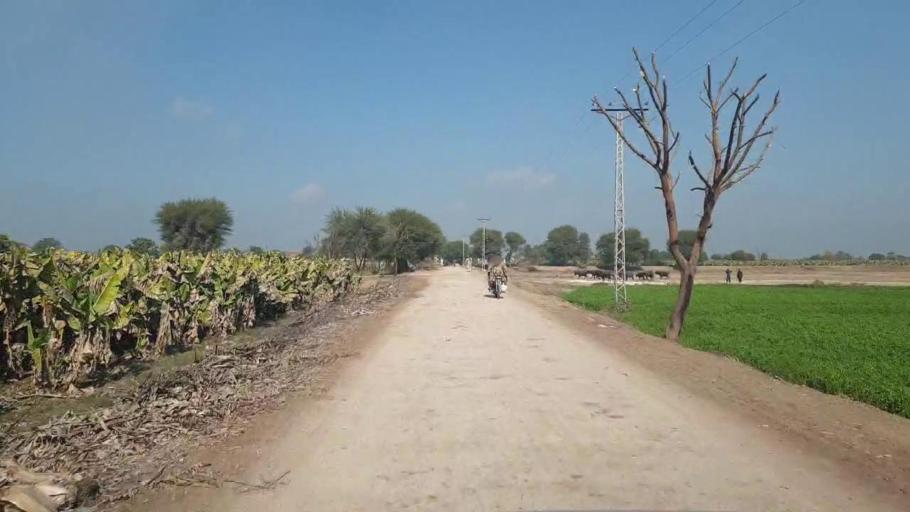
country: PK
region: Sindh
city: Shahdadpur
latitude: 25.9289
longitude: 68.5858
